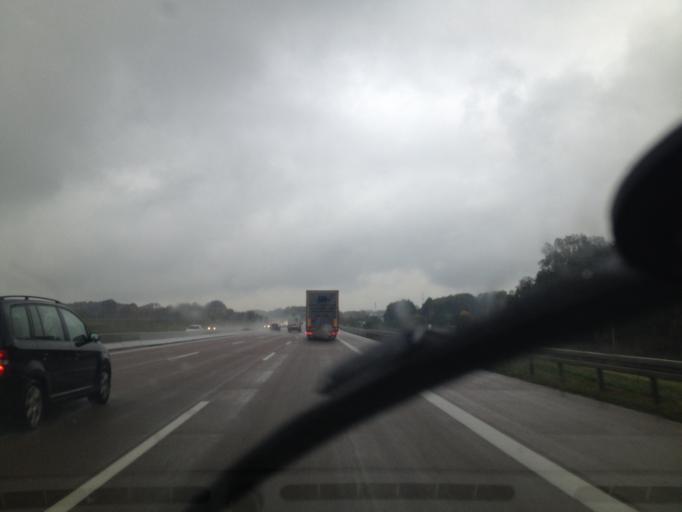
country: DE
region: Bavaria
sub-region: Swabia
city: Rettenbach
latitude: 48.4349
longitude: 10.3343
